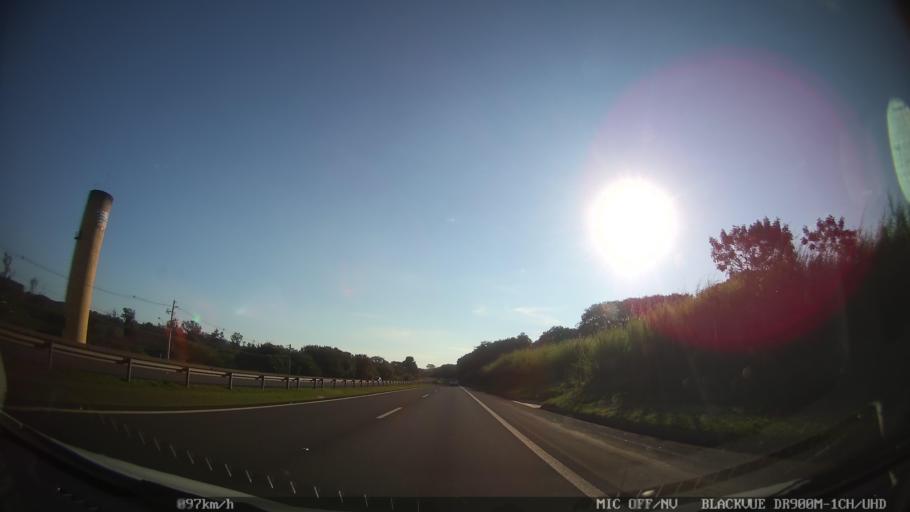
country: BR
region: Sao Paulo
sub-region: Piracicaba
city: Piracicaba
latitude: -22.6979
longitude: -47.6122
